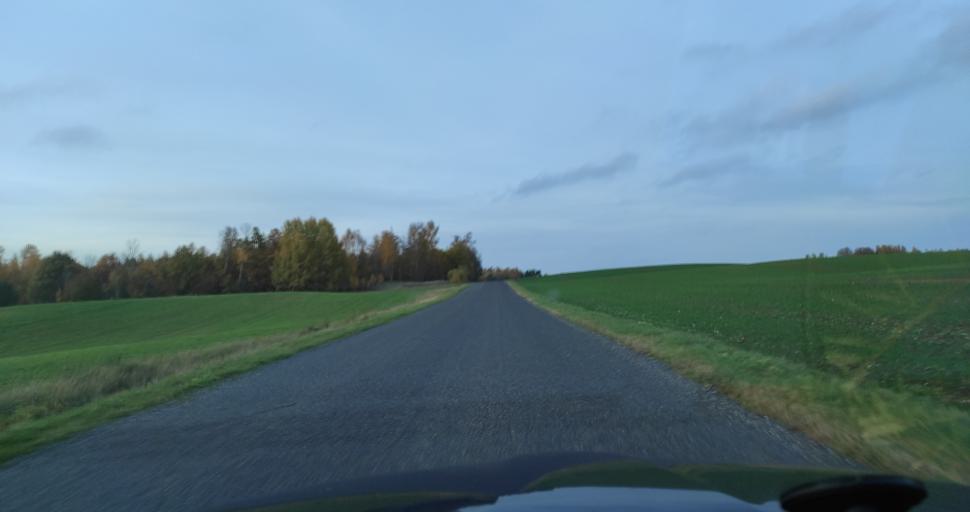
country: LV
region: Aizpute
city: Aizpute
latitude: 56.7050
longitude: 21.7939
